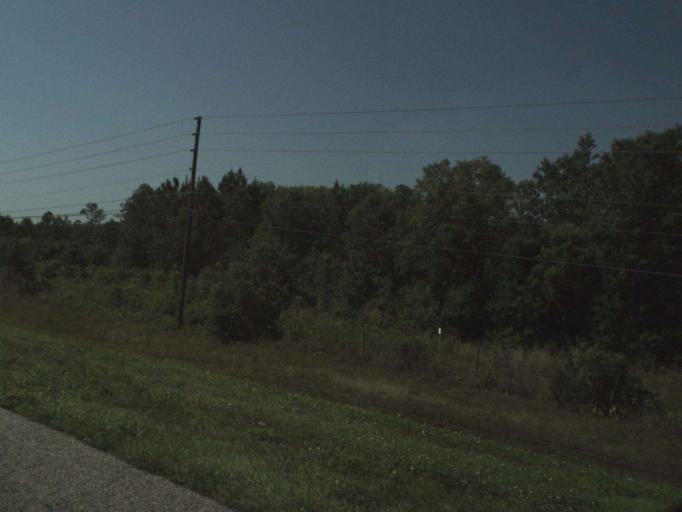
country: US
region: Florida
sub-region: Orange County
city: Wedgefield
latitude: 28.4999
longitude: -81.0496
